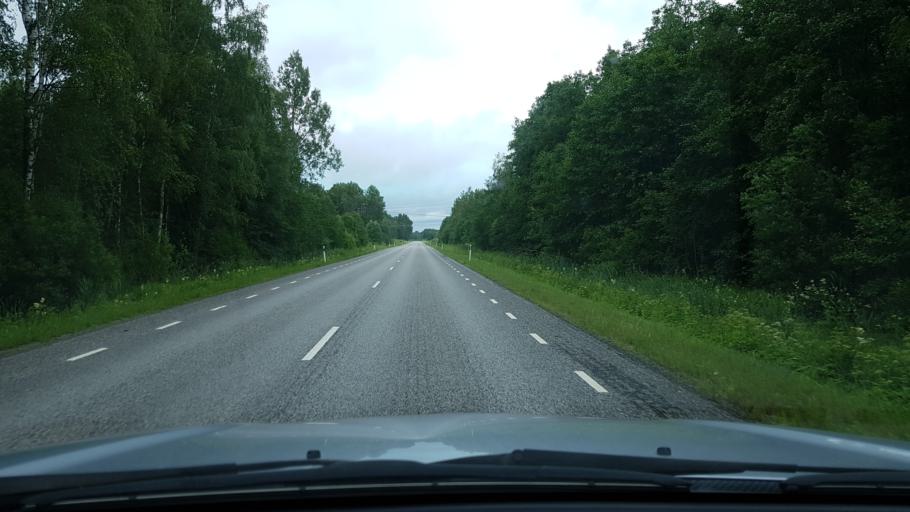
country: EE
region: Ida-Virumaa
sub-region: Narva-Joesuu linn
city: Narva-Joesuu
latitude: 59.3541
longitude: 27.9279
